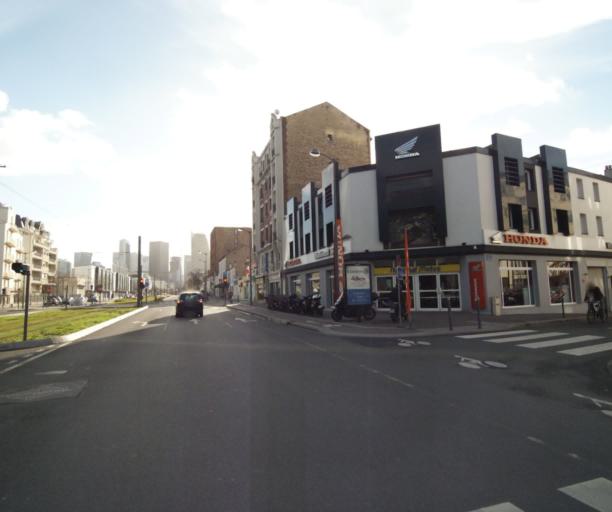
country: FR
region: Ile-de-France
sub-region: Departement des Hauts-de-Seine
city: La Garenne-Colombes
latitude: 48.9051
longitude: 2.2391
